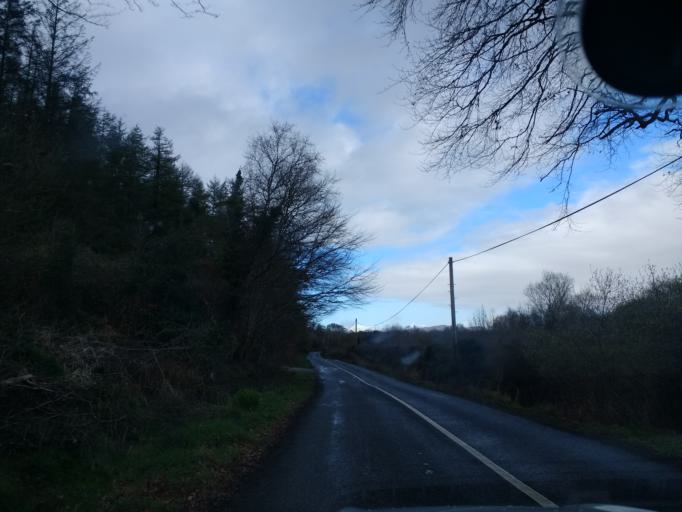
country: IE
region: Ulster
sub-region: County Donegal
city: Buncrana
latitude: 55.1231
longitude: -7.5284
